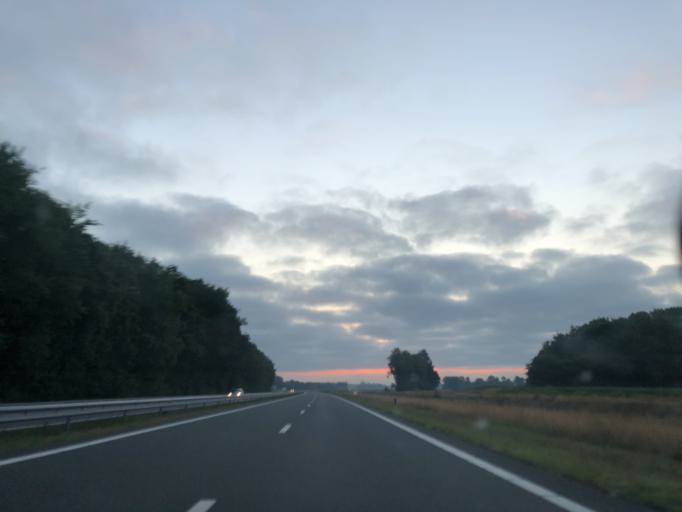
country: NL
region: Drenthe
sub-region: Gemeente Aa en Hunze
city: Anloo
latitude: 53.0155
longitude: 6.7673
